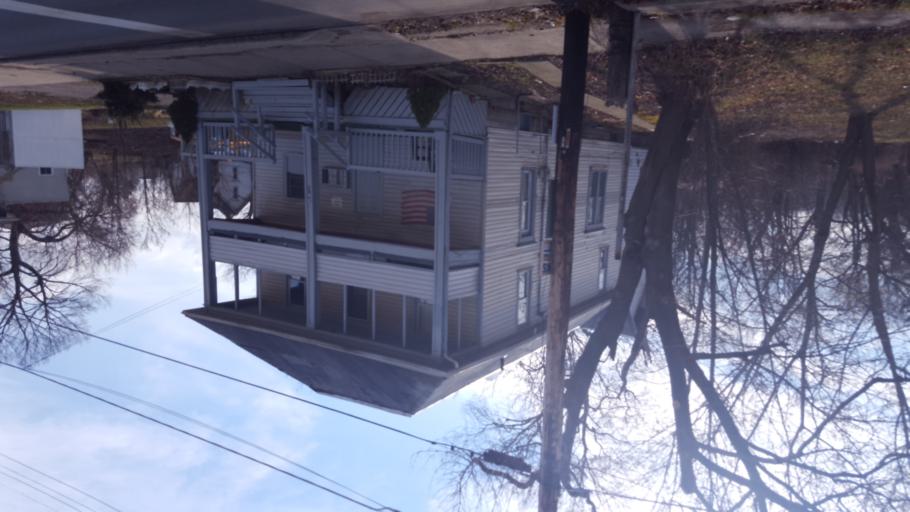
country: US
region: Ohio
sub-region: Richland County
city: Mansfield
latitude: 40.7678
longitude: -82.5188
